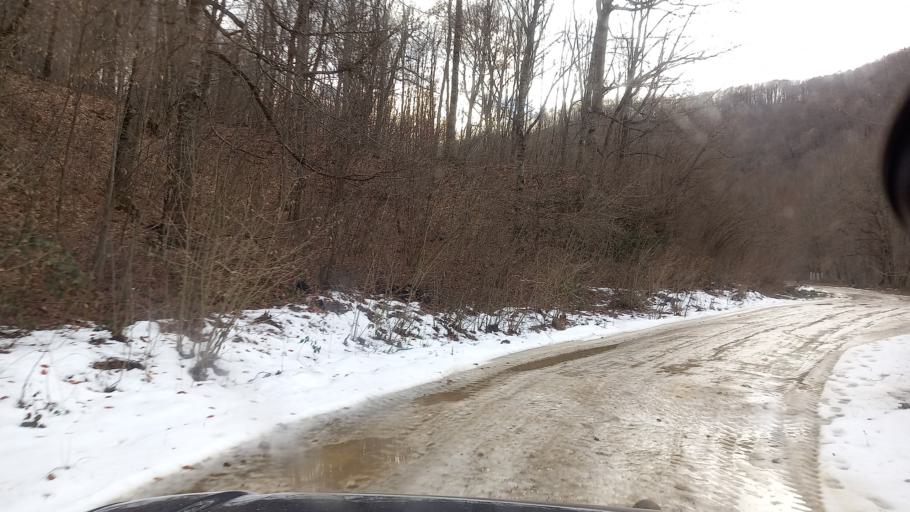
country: RU
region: Adygeya
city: Kamennomostskiy
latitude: 44.1626
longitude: 40.2986
